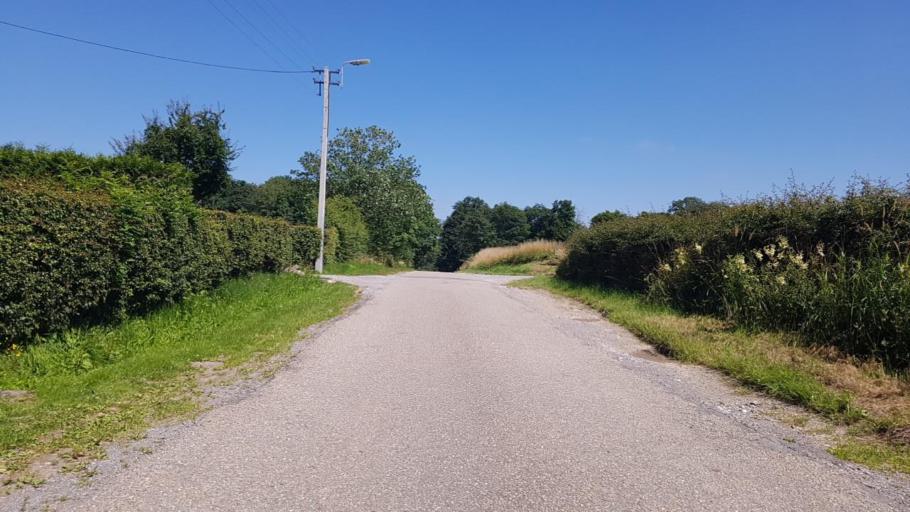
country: BE
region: Wallonia
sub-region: Province du Hainaut
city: Froidchapelle
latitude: 50.1191
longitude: 4.2486
